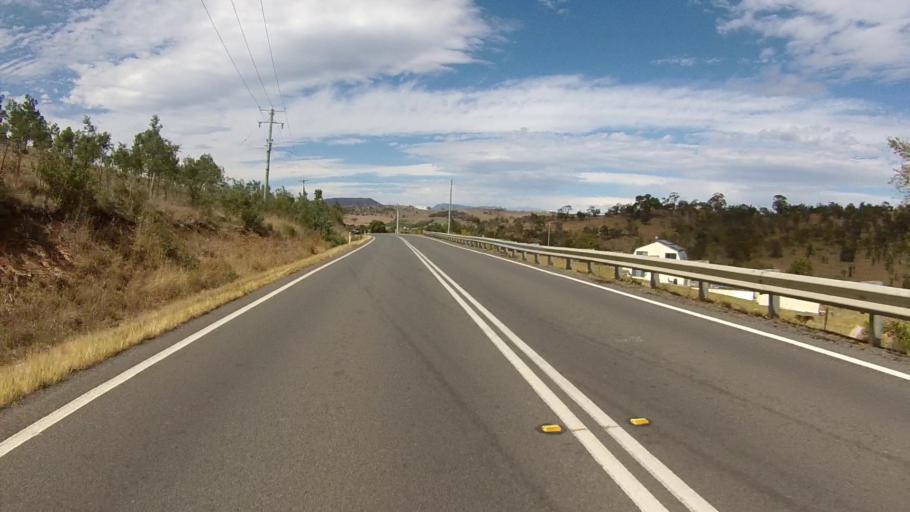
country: AU
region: Tasmania
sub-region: Brighton
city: Old Beach
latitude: -42.6800
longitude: 147.3539
